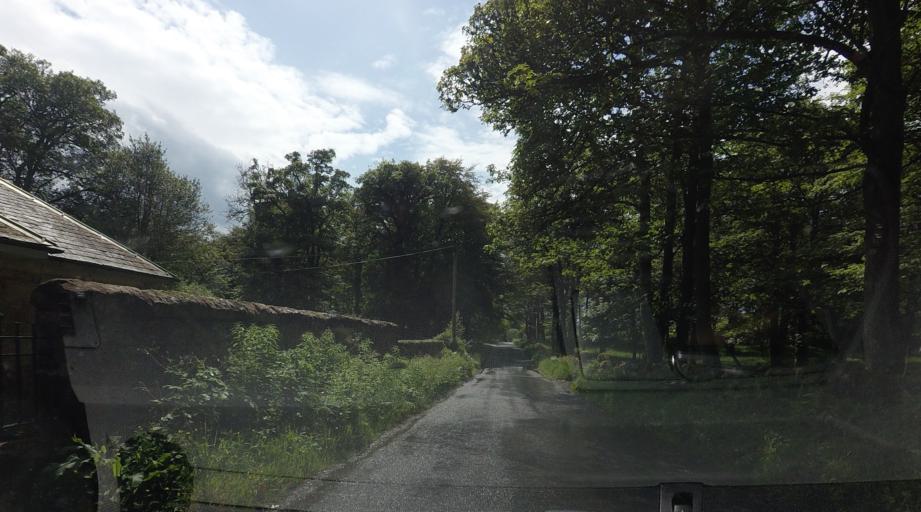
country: GB
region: Scotland
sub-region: Fife
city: Ballingry
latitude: 56.1564
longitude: -3.3611
